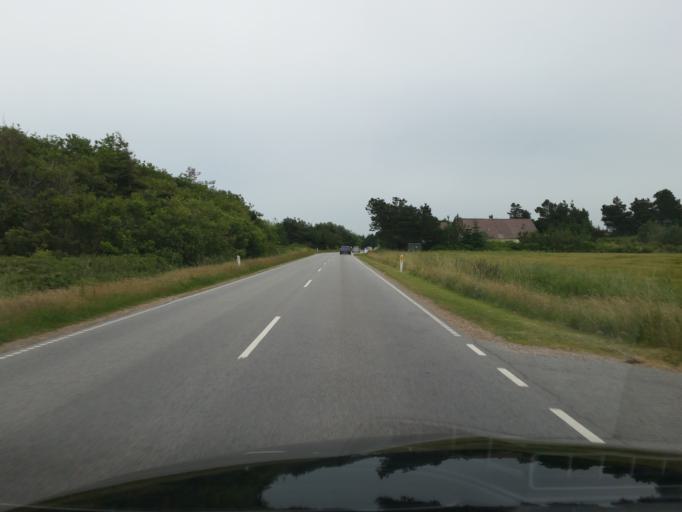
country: DK
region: South Denmark
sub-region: Varde Kommune
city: Oksbol
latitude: 55.8092
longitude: 8.2194
